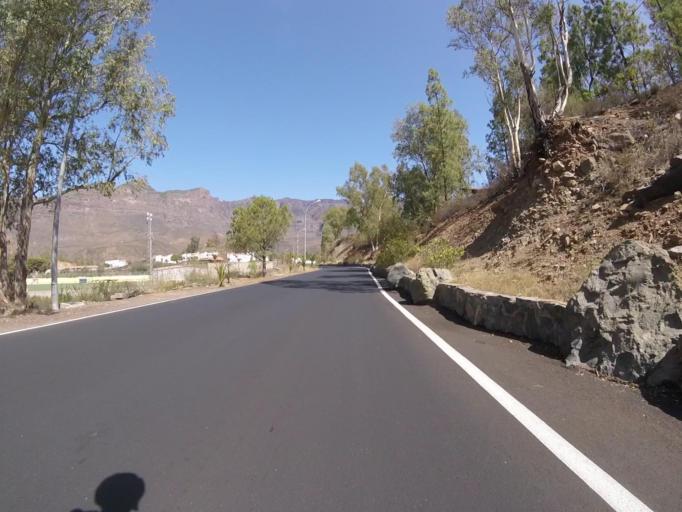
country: ES
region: Canary Islands
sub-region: Provincia de Las Palmas
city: San Bartolome
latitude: 27.9198
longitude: -15.5750
